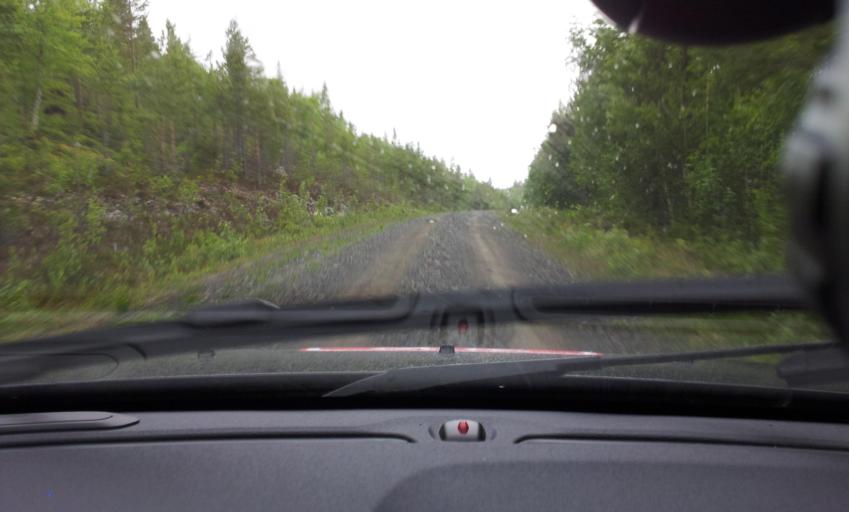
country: SE
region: Jaemtland
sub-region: Are Kommun
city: Jarpen
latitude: 63.1914
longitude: 13.4324
